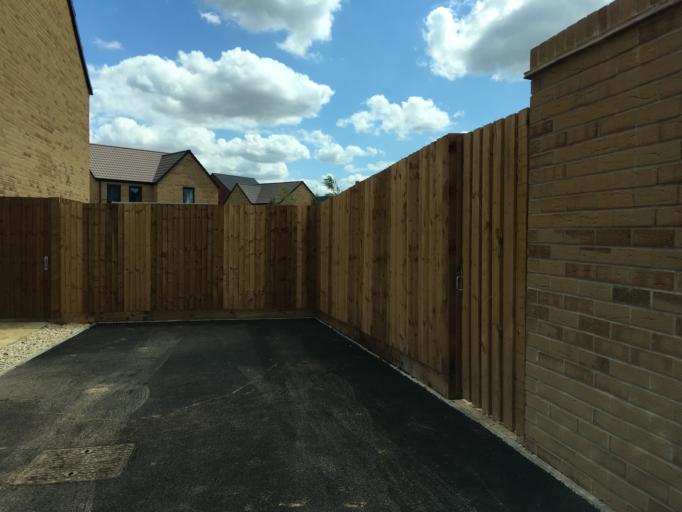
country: GB
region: England
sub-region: South Gloucestershire
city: Yate
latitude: 51.5579
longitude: -2.4179
